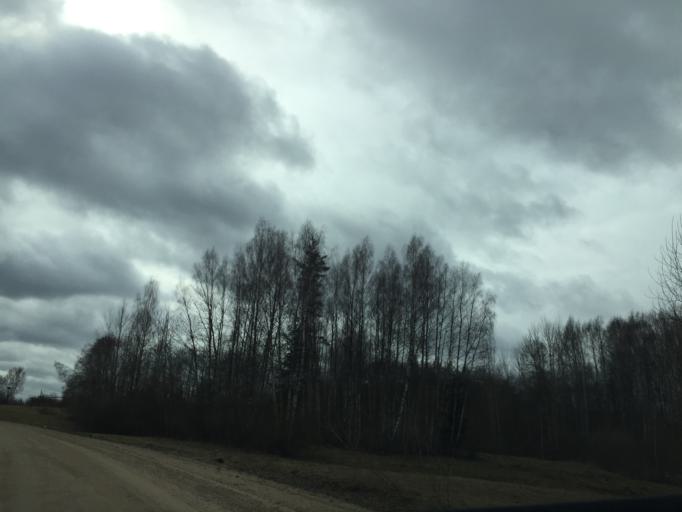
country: LV
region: Kraslavas Rajons
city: Kraslava
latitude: 55.9728
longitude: 27.0781
